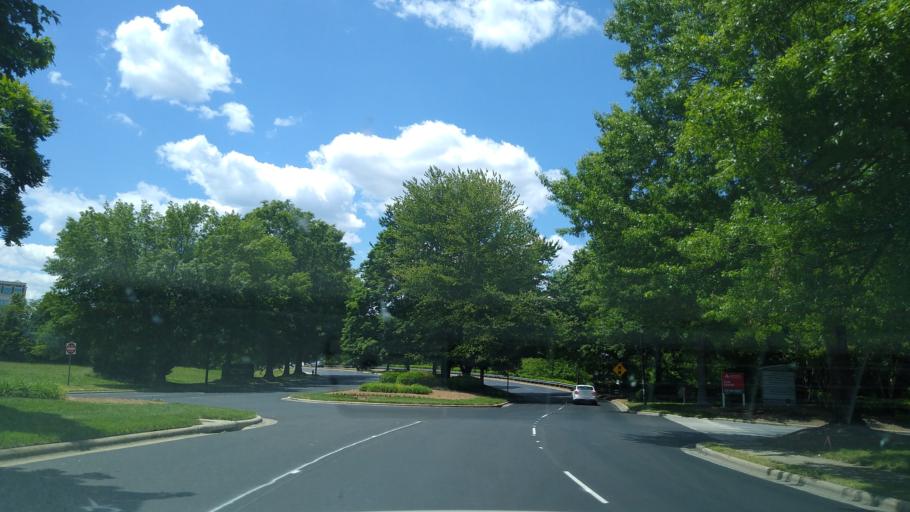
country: US
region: North Carolina
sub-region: Guilford County
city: Greensboro
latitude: 36.0896
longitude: -79.8234
